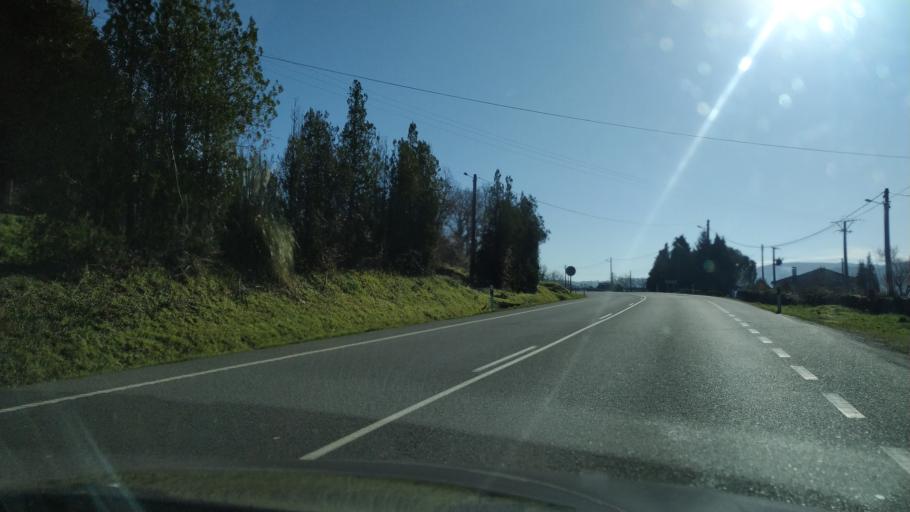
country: ES
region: Galicia
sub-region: Provincia da Coruna
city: Ribeira
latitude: 42.7539
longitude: -8.3866
